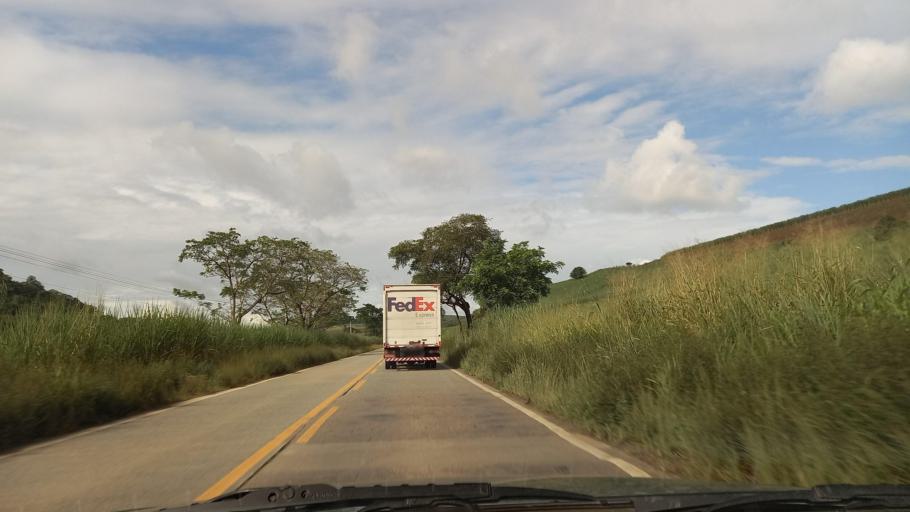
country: BR
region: Pernambuco
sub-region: Catende
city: Catende
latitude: -8.6950
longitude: -35.6886
